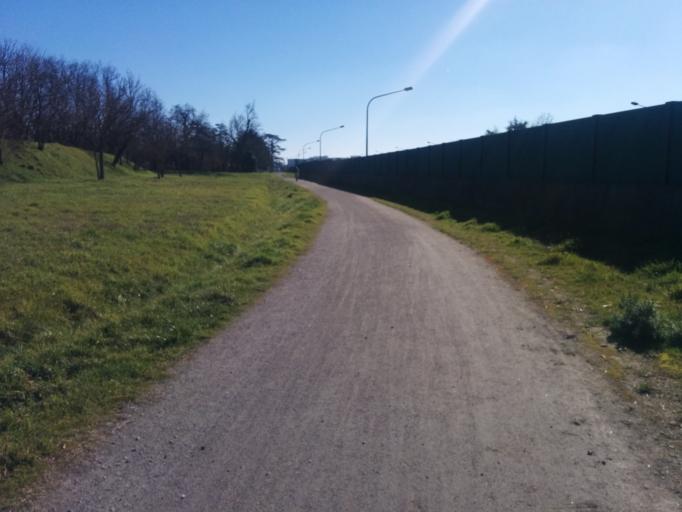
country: FR
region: Midi-Pyrenees
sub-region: Departement de la Haute-Garonne
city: Colomiers
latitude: 43.5835
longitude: 1.3638
